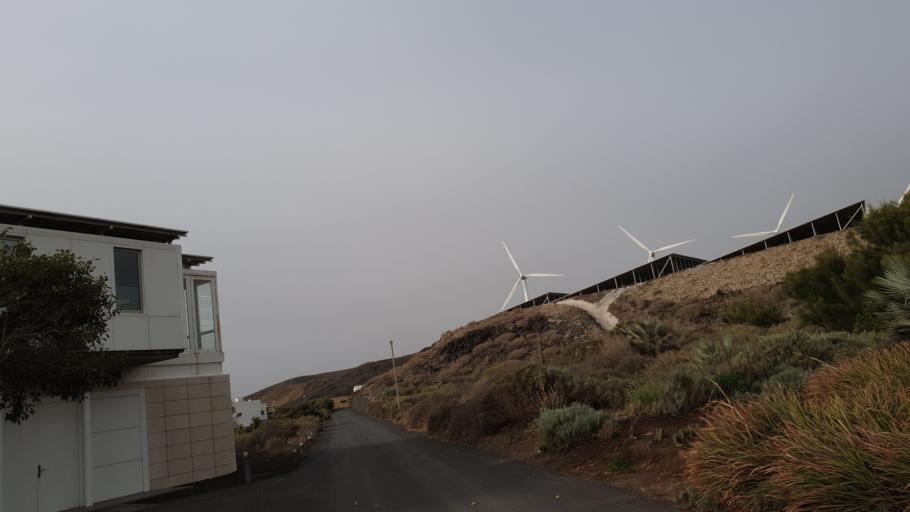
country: ES
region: Canary Islands
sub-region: Provincia de Santa Cruz de Tenerife
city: San Isidro
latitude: 28.0694
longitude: -16.5091
